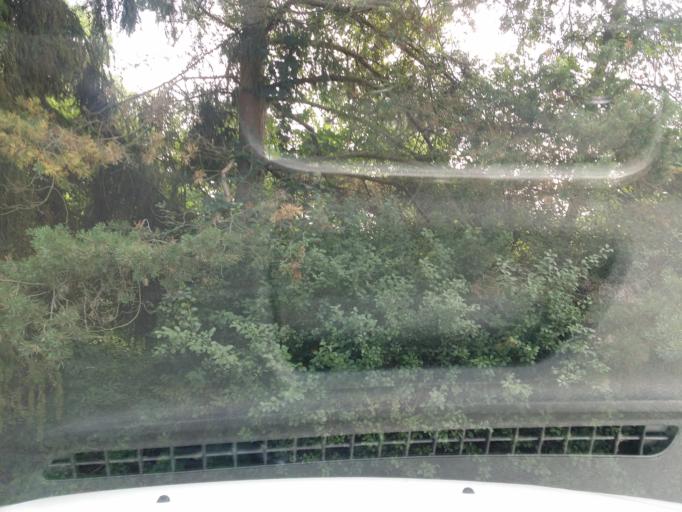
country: HU
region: Borsod-Abauj-Zemplen
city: Satoraljaujhely
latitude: 48.4585
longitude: 21.5906
